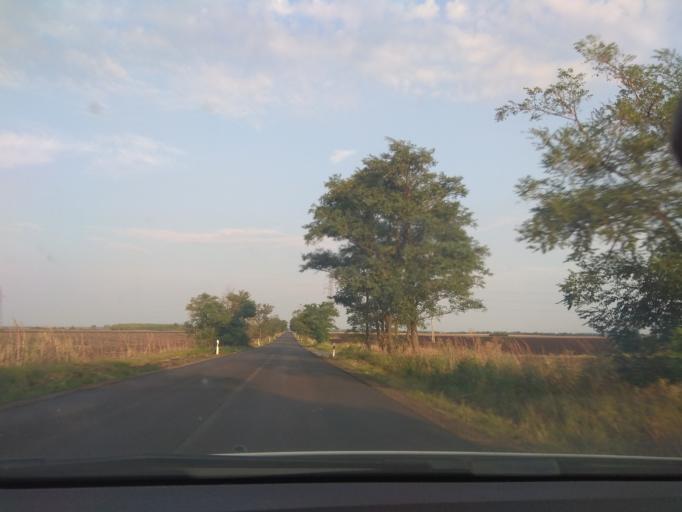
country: HU
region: Borsod-Abauj-Zemplen
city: Mezokovesd
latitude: 47.8146
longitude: 20.5238
